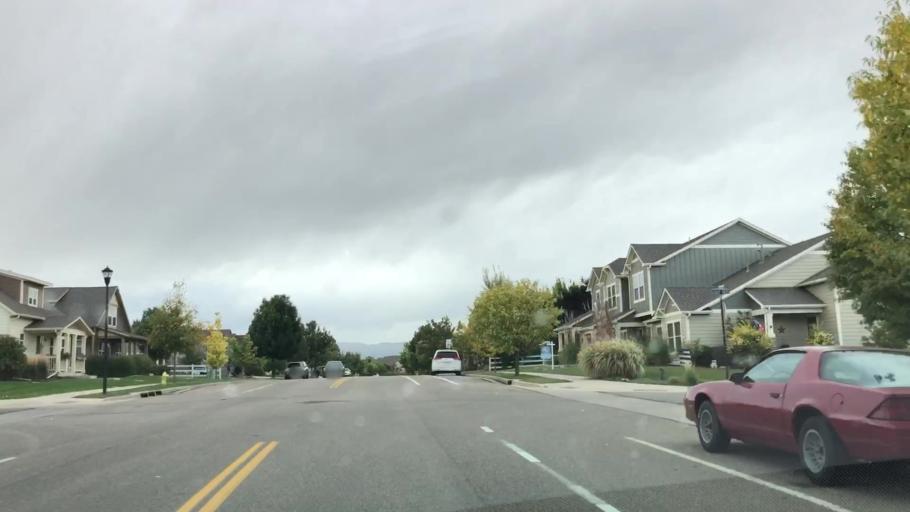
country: US
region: Colorado
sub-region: Larimer County
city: Fort Collins
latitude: 40.5455
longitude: -105.0242
